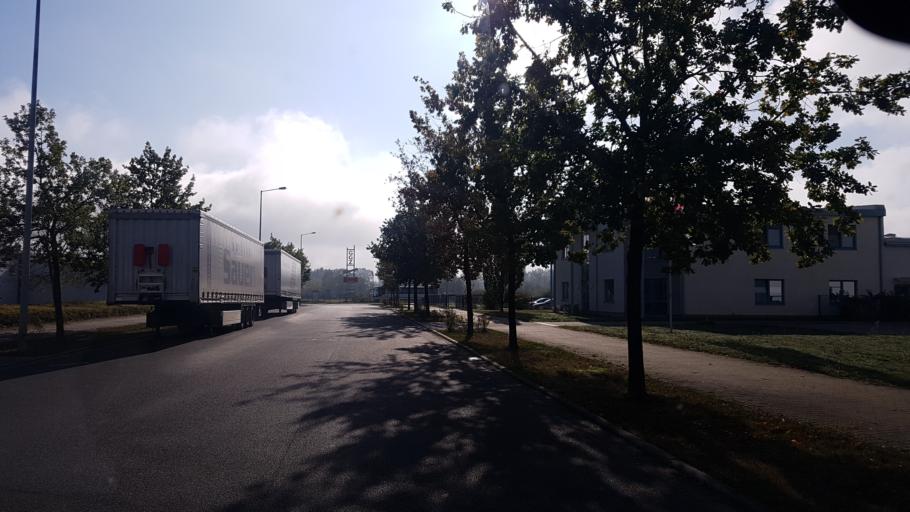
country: DE
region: Brandenburg
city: Elsterwerda
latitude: 51.4616
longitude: 13.5381
